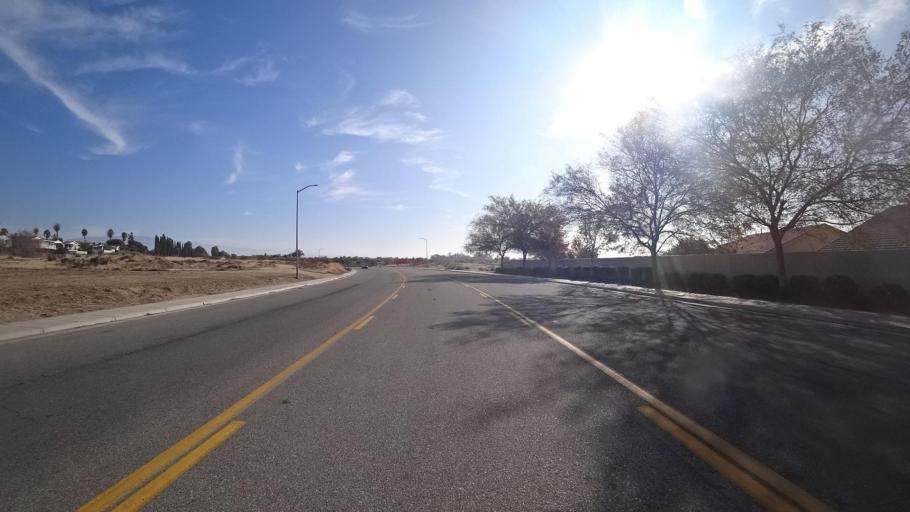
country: US
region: California
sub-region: Kern County
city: Bakersfield
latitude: 35.3758
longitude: -118.9079
